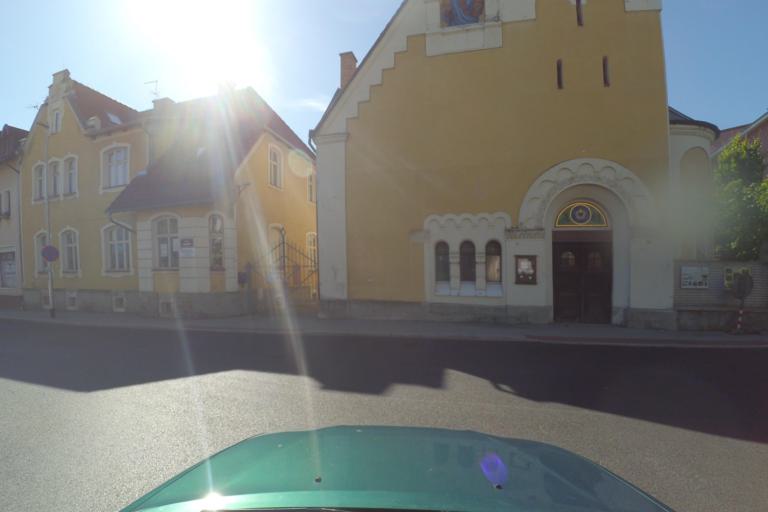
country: CZ
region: Karlovarsky
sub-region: Okres Sokolov
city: Sokolov
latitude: 50.1816
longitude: 12.6435
